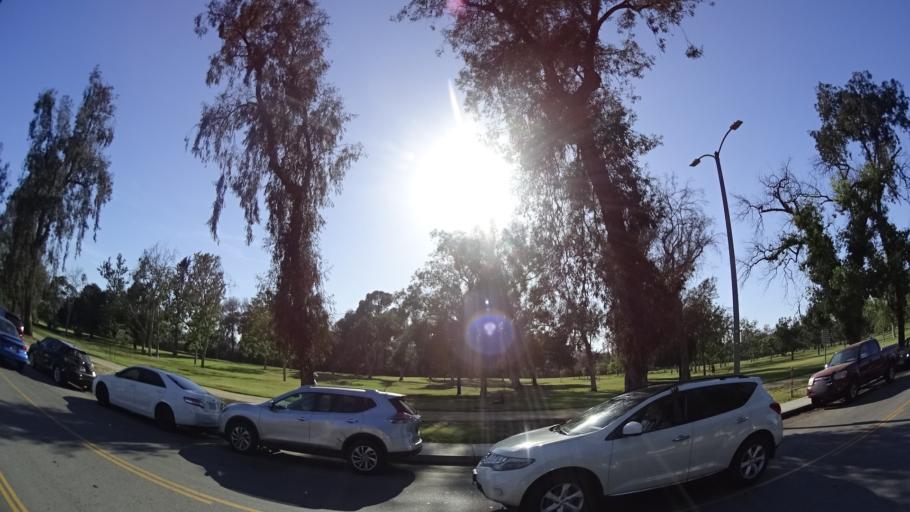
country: US
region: California
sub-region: Los Angeles County
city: North Hollywood
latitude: 34.1616
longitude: -118.3790
